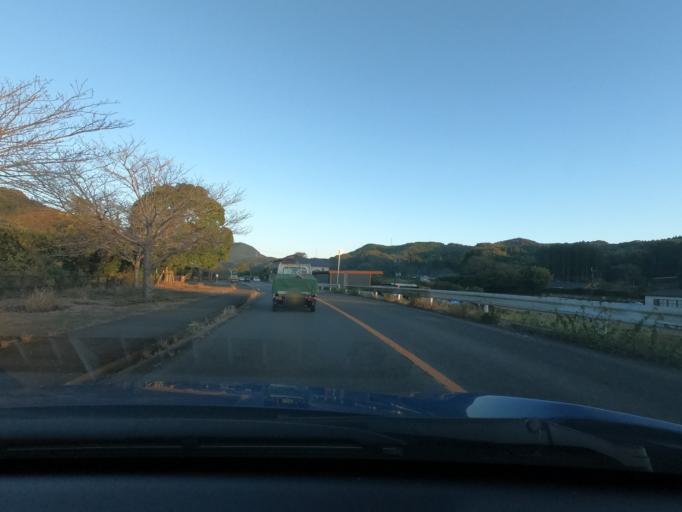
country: JP
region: Kagoshima
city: Satsumasendai
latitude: 31.7921
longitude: 130.4517
